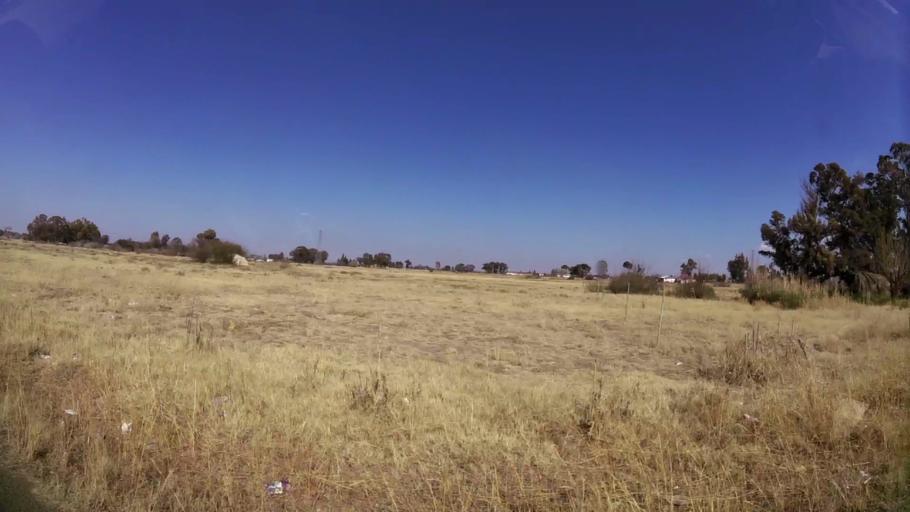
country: ZA
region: Orange Free State
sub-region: Mangaung Metropolitan Municipality
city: Bloemfontein
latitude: -29.1553
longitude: 26.3066
